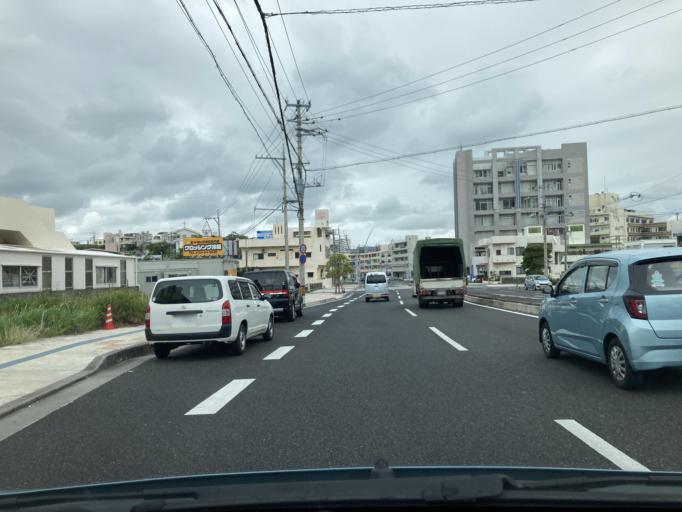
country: JP
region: Okinawa
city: Tomigusuku
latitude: 26.1973
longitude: 127.7269
